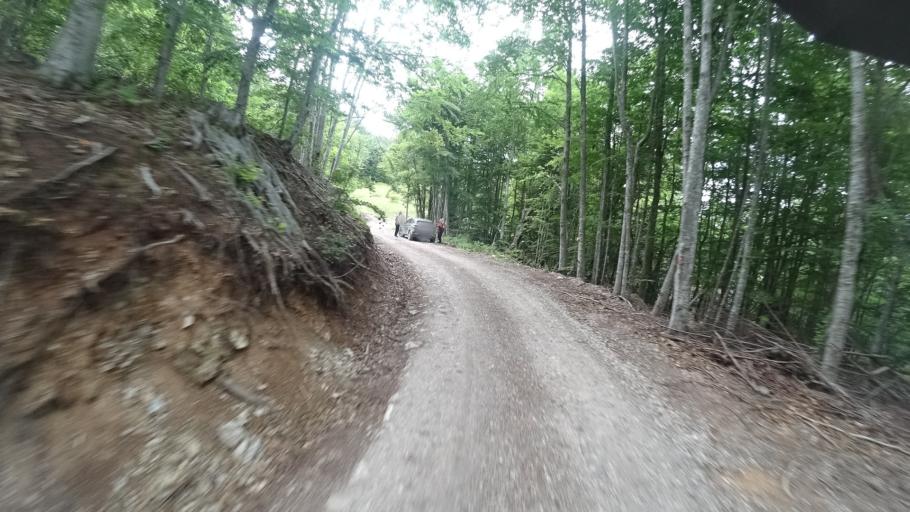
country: HR
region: Zadarska
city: Obrovac
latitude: 44.2891
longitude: 15.6753
